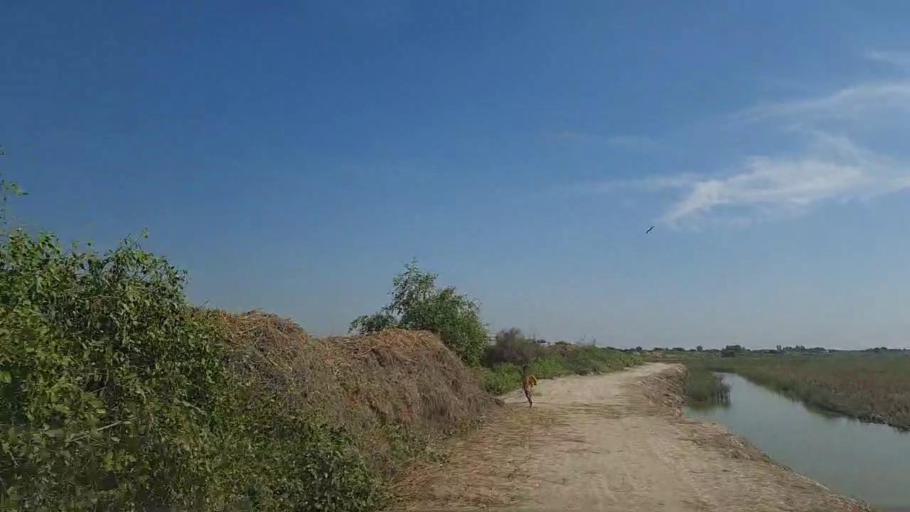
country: PK
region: Sindh
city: Mirpur Batoro
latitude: 24.7550
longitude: 68.3034
